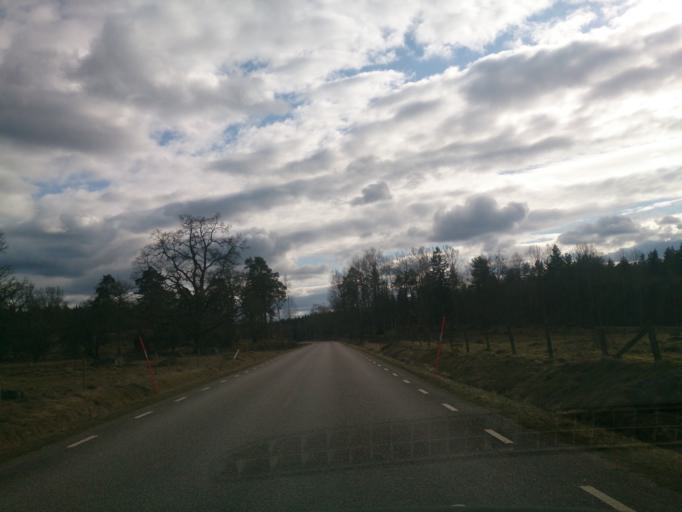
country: SE
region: OEstergoetland
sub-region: Atvidabergs Kommun
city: Atvidaberg
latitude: 58.3299
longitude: 16.0270
